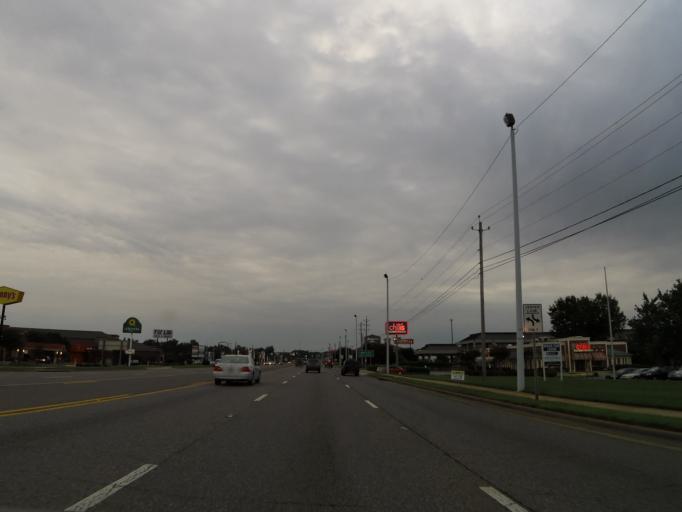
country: US
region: Alabama
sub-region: Madison County
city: Redstone Arsenal
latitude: 34.7378
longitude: -86.6557
